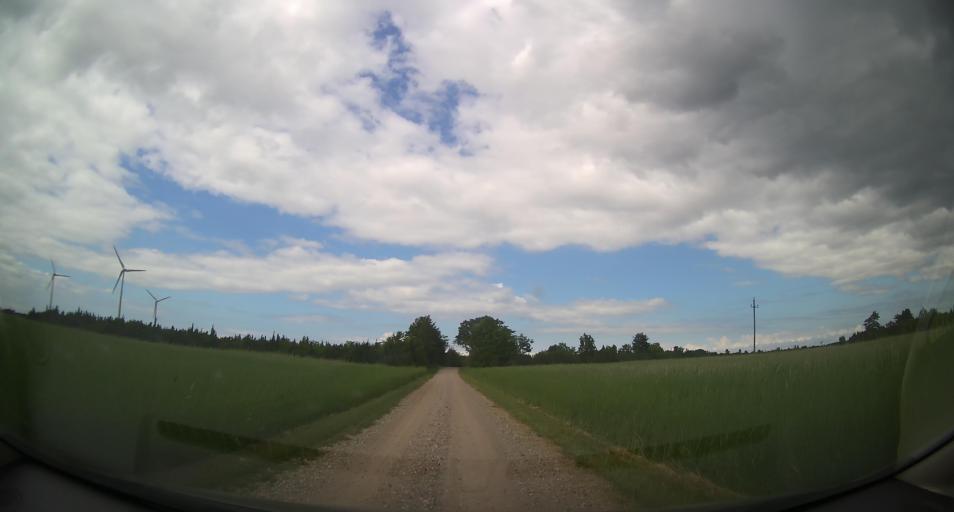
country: EE
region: Laeaene
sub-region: Lihula vald
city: Lihula
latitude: 58.5648
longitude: 23.5480
